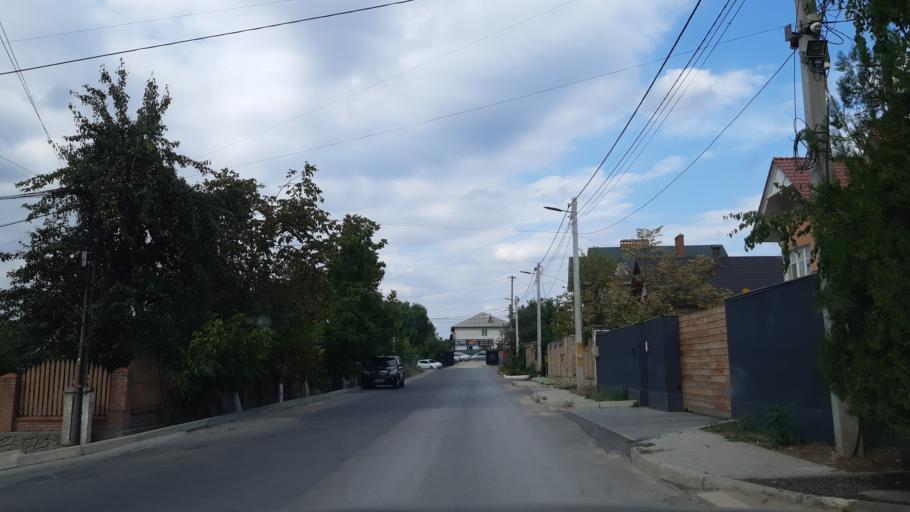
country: MD
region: Chisinau
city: Vatra
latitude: 47.0481
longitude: 28.7379
